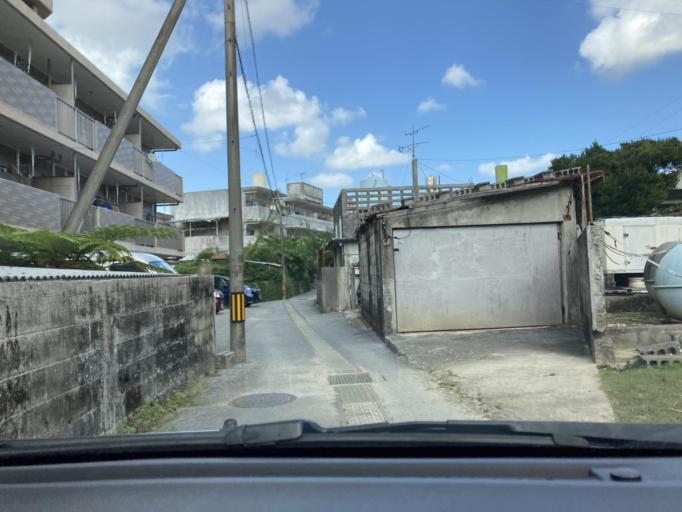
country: JP
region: Okinawa
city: Naha-shi
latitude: 26.2094
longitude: 127.7121
